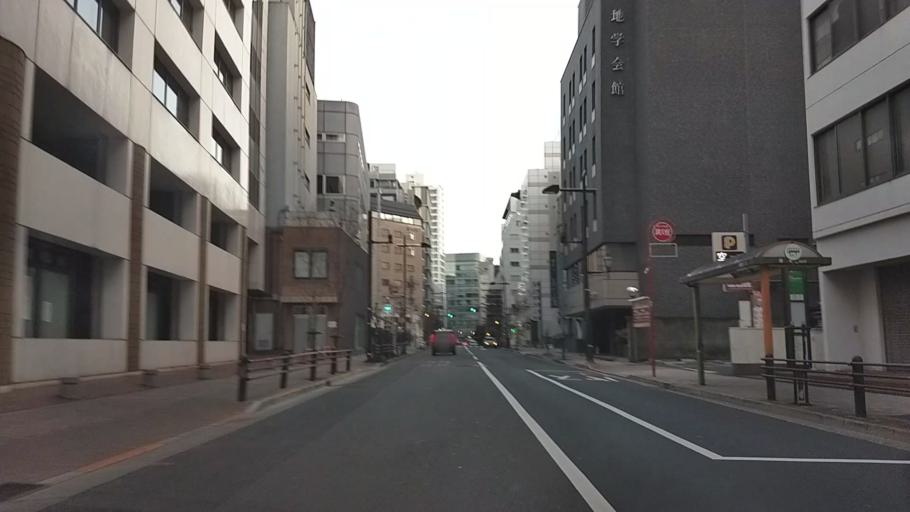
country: JP
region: Tokyo
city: Tokyo
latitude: 35.6876
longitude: 139.7362
